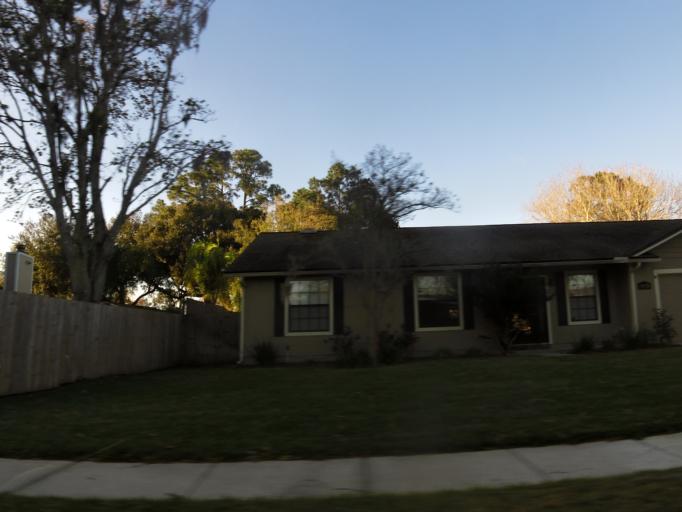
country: US
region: Florida
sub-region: Saint Johns County
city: Fruit Cove
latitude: 30.1764
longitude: -81.5822
